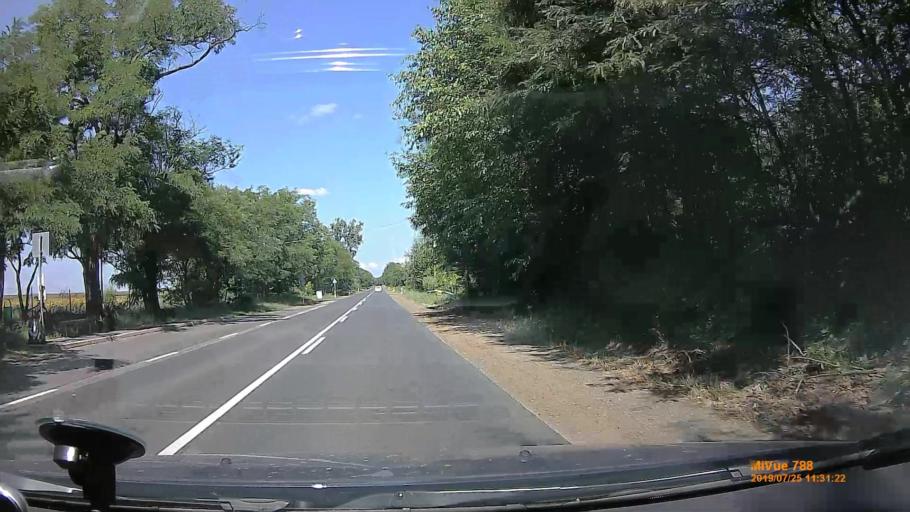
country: HU
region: Szabolcs-Szatmar-Bereg
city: Nagykallo
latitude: 47.9059
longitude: 21.7847
